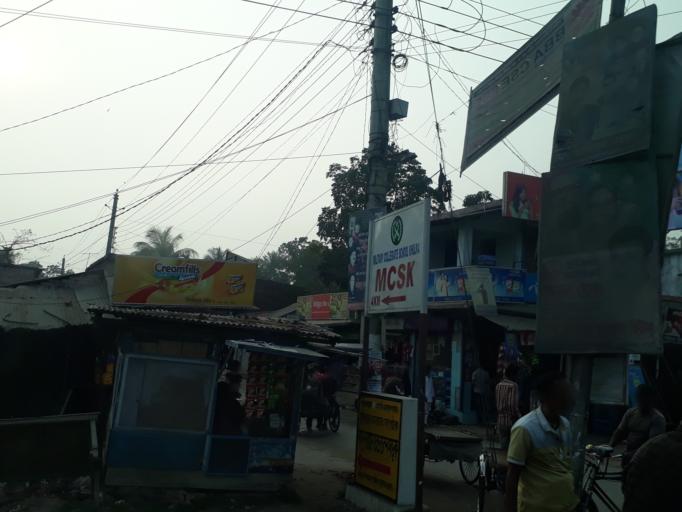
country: BD
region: Khulna
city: Bhatpara Abhaynagar
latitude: 22.9476
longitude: 89.4796
